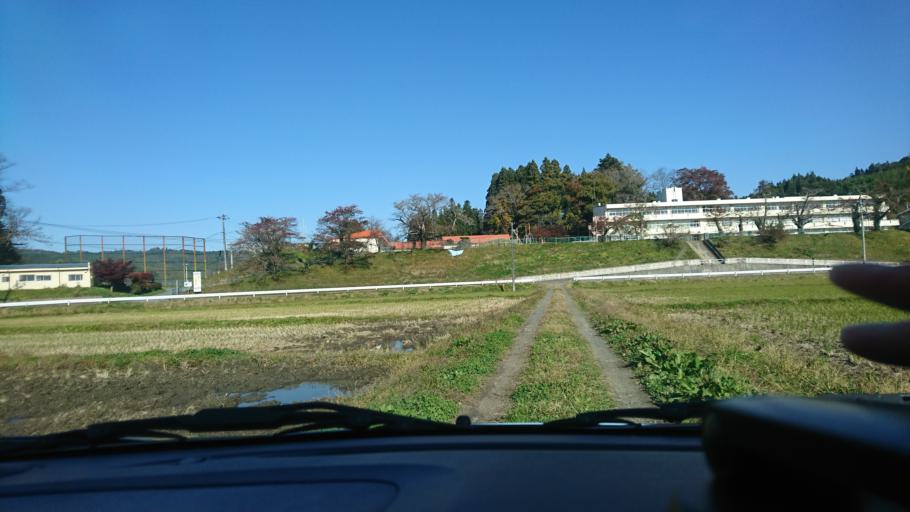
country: JP
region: Iwate
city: Ichinoseki
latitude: 38.8506
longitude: 141.2894
